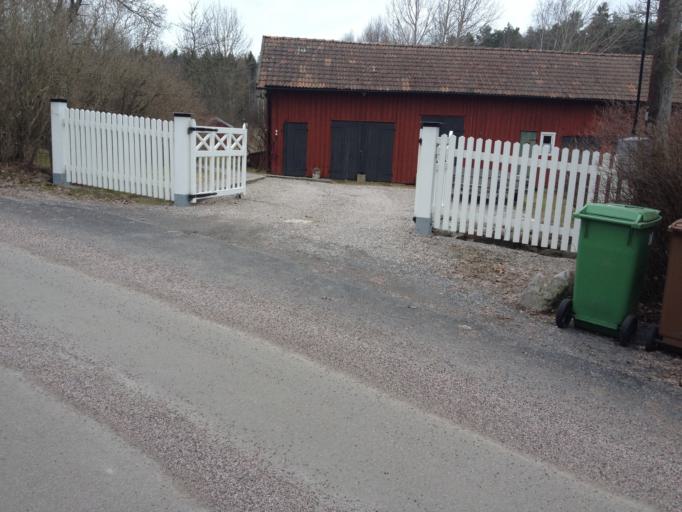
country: SE
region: Vaestmanland
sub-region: Kopings Kommun
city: Koping
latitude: 59.5138
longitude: 16.0187
